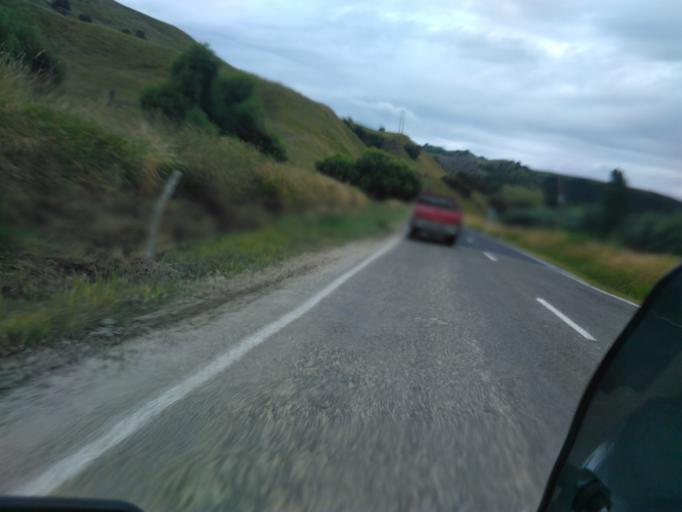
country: NZ
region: Gisborne
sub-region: Gisborne District
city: Gisborne
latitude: -38.4592
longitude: 177.7460
